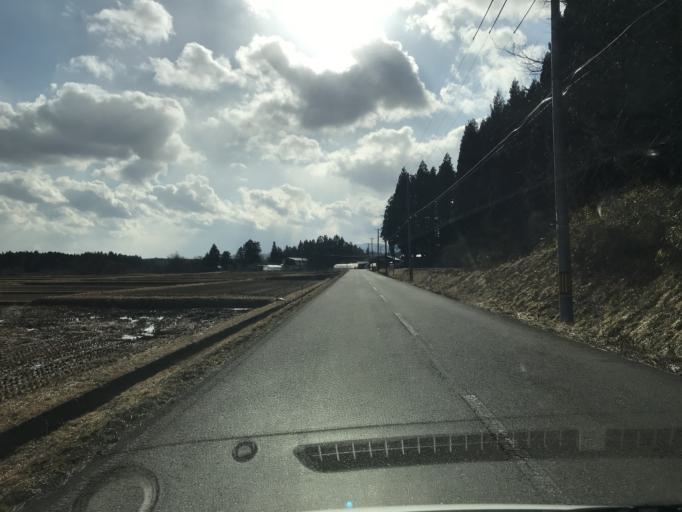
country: JP
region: Iwate
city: Mizusawa
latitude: 39.1477
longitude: 141.0408
